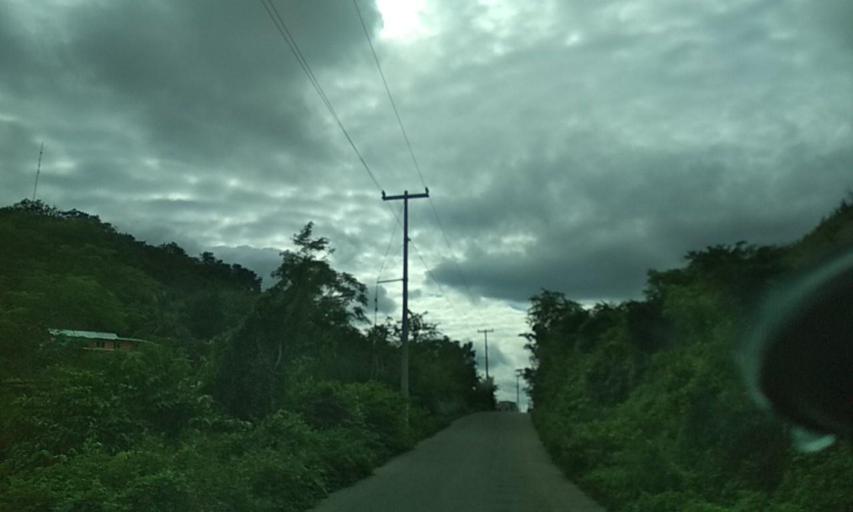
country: MX
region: Veracruz
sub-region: Papantla
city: Polutla
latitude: 20.5362
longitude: -97.2325
